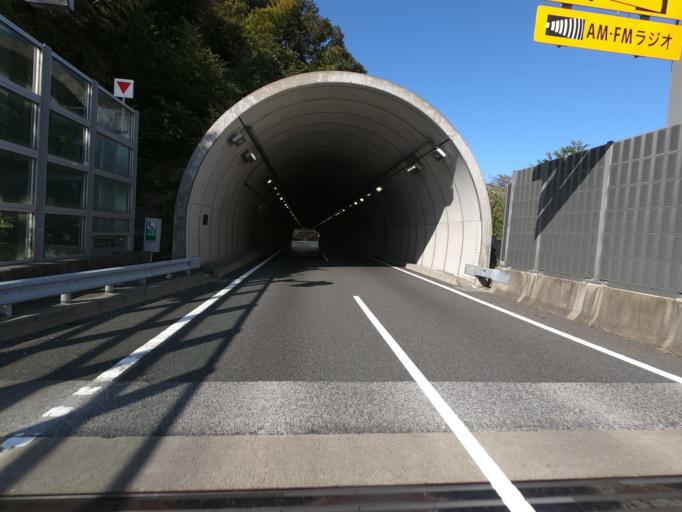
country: JP
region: Kanagawa
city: Zama
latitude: 35.5094
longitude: 139.3642
